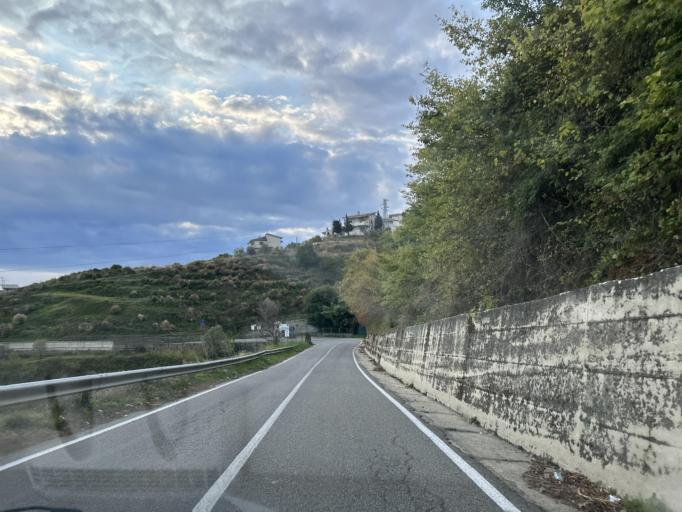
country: IT
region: Calabria
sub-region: Provincia di Catanzaro
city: Montauro
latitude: 38.7507
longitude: 16.5080
